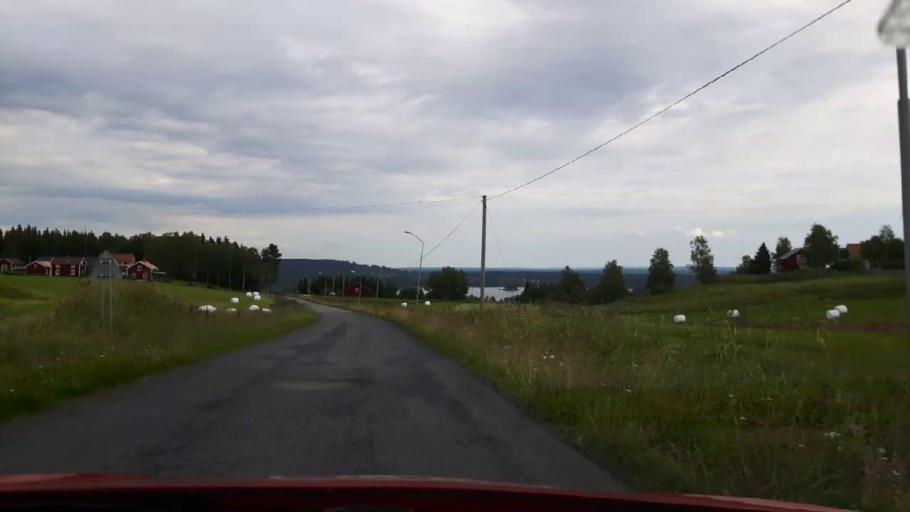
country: SE
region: Jaemtland
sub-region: Stroemsunds Kommun
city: Stroemsund
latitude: 63.5242
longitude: 15.3565
